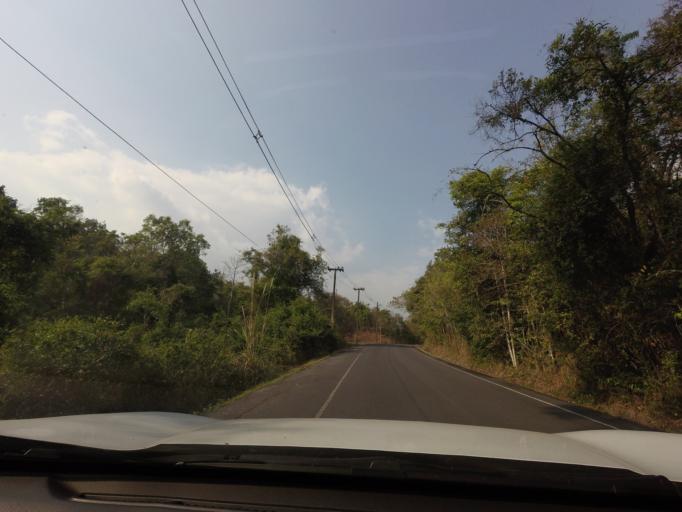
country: TH
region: Nakhon Ratchasima
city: Pak Chong
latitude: 14.4287
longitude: 101.3931
